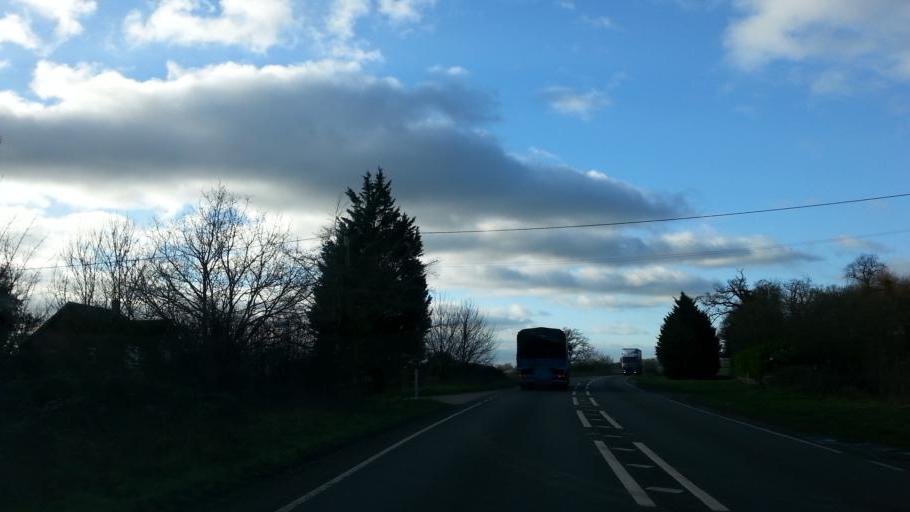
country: GB
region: England
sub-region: Norfolk
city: Harleston
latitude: 52.3643
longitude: 1.2109
